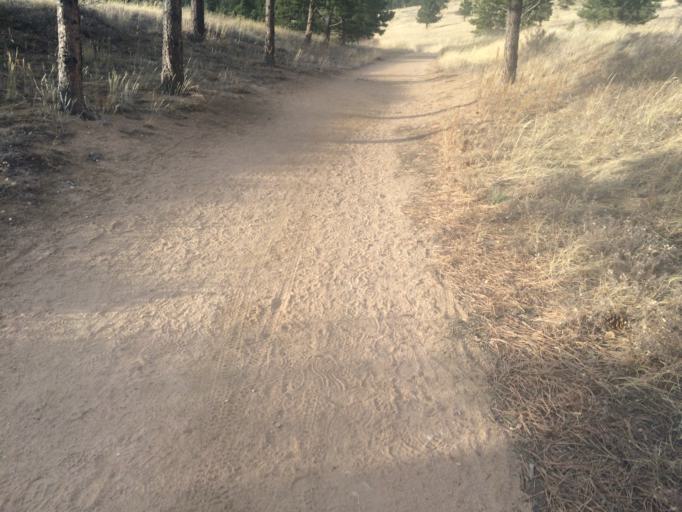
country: US
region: Colorado
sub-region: Boulder County
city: Coal Creek
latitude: 39.9586
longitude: -105.3418
